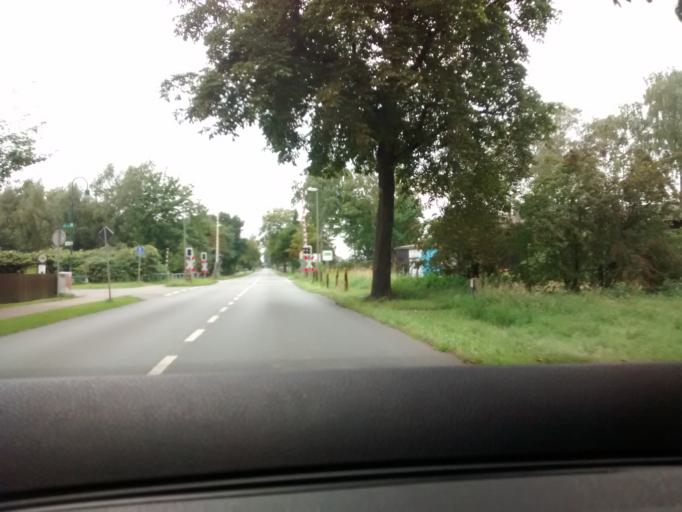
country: DE
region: Lower Saxony
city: Echem
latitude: 53.3388
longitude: 10.5408
